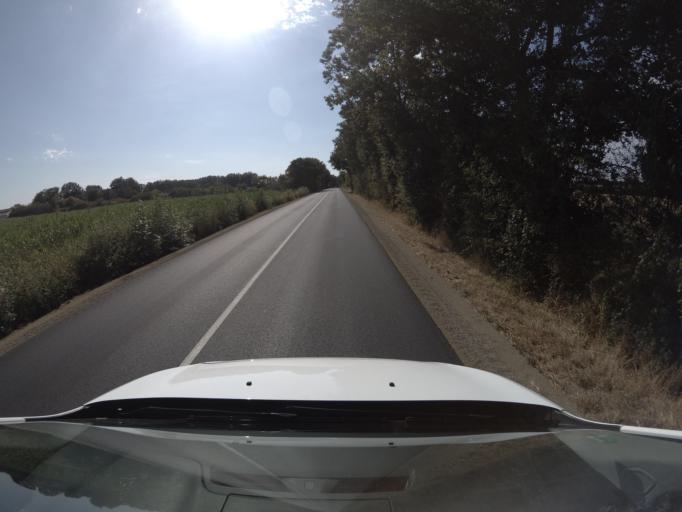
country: FR
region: Poitou-Charentes
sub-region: Departement des Deux-Sevres
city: Mauze-Thouarsais
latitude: 46.9993
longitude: -0.3248
